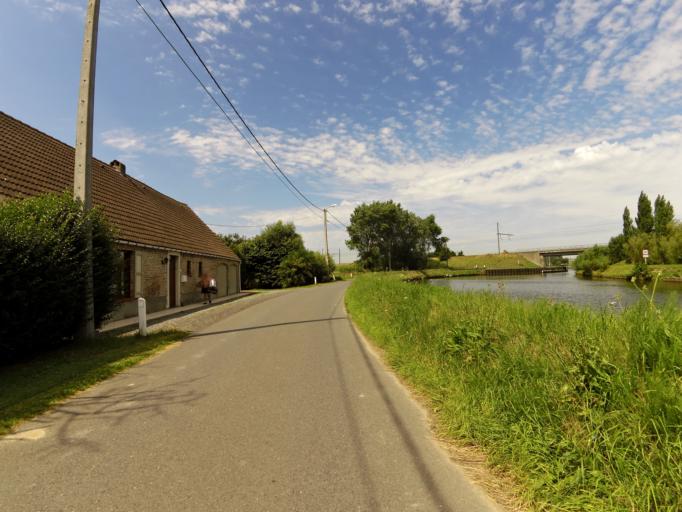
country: BE
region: Flanders
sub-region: Provincie West-Vlaanderen
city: Oudenburg
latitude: 51.2051
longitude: 3.0030
